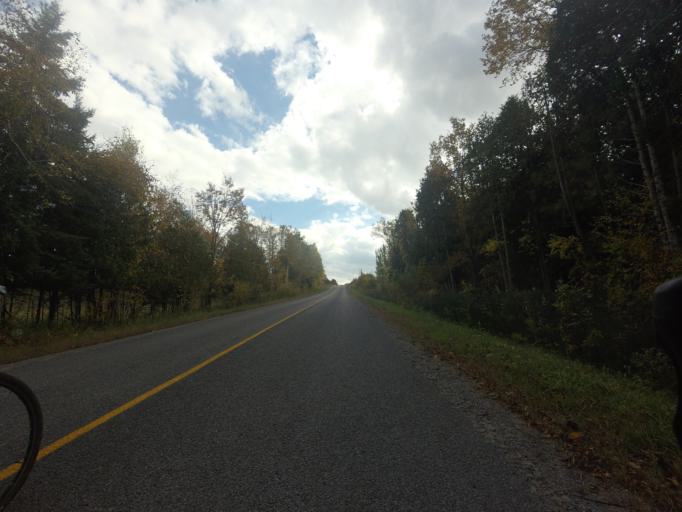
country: CA
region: Ontario
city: Pembroke
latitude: 45.5776
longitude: -77.1303
